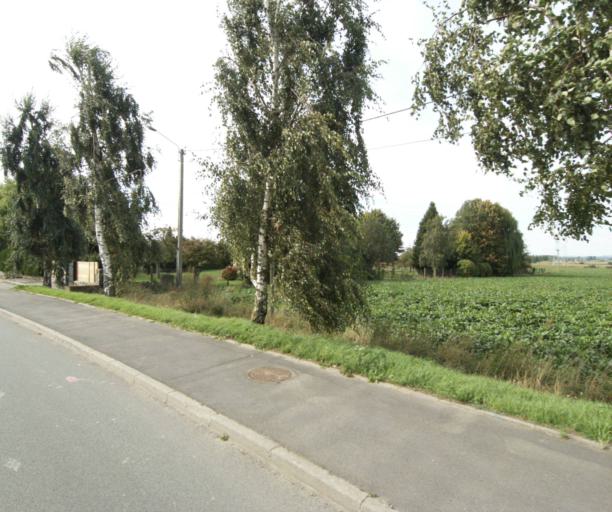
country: FR
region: Nord-Pas-de-Calais
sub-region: Departement du Nord
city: Radinghem-en-Weppes
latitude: 50.6185
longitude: 2.9260
